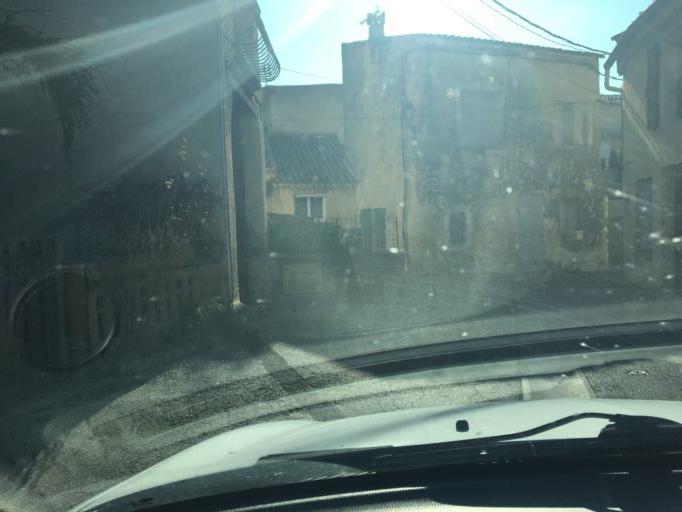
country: FR
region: Provence-Alpes-Cote d'Azur
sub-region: Departement des Bouches-du-Rhone
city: Mallemort
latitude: 43.7326
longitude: 5.1808
